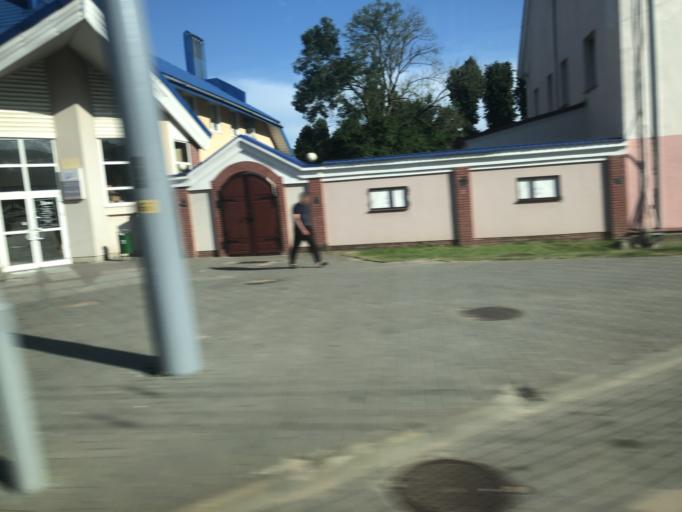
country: BY
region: Grodnenskaya
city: Hrodna
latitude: 53.6561
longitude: 23.8016
